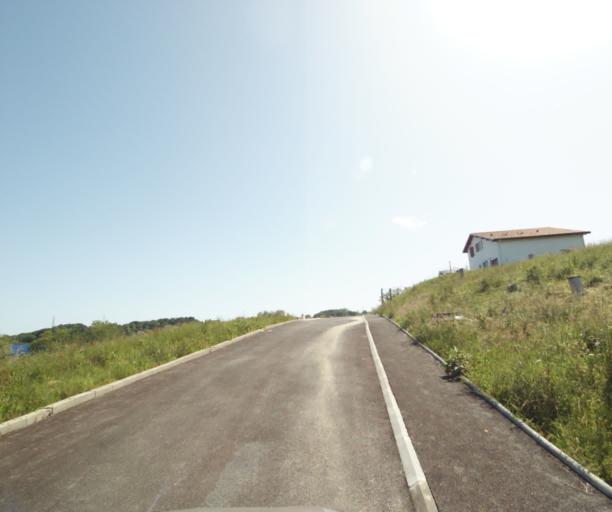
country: FR
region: Aquitaine
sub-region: Departement des Pyrenees-Atlantiques
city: Mouguerre
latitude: 43.4761
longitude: -1.4468
